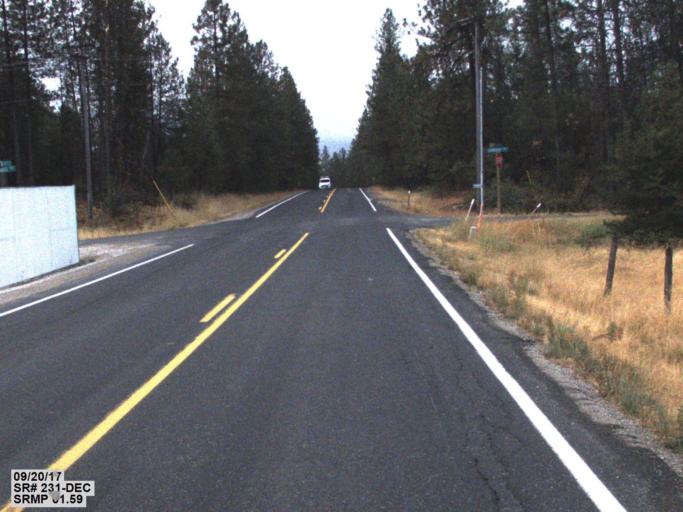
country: US
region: Washington
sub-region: Stevens County
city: Chewelah
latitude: 48.0487
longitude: -117.7415
